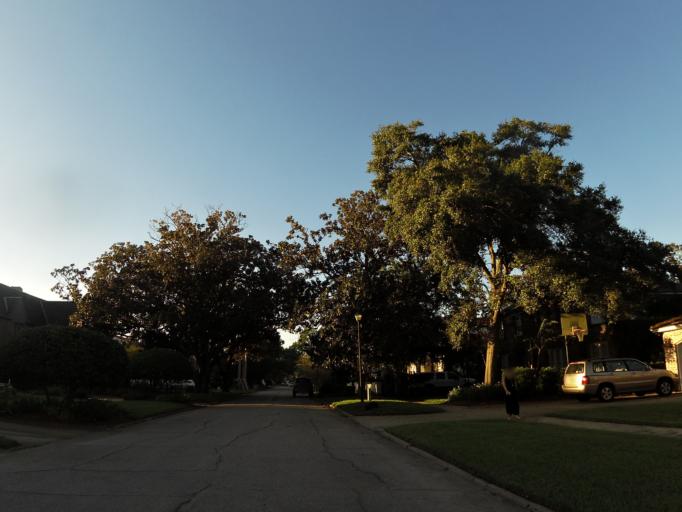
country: US
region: Florida
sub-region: Duval County
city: Jacksonville
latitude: 30.3032
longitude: -81.6584
